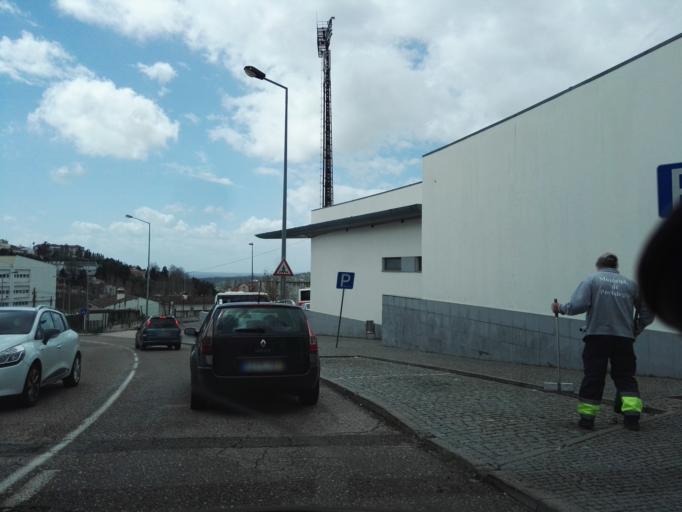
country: PT
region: Portalegre
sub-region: Portalegre
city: Portalegre
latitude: 39.2975
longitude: -7.4324
